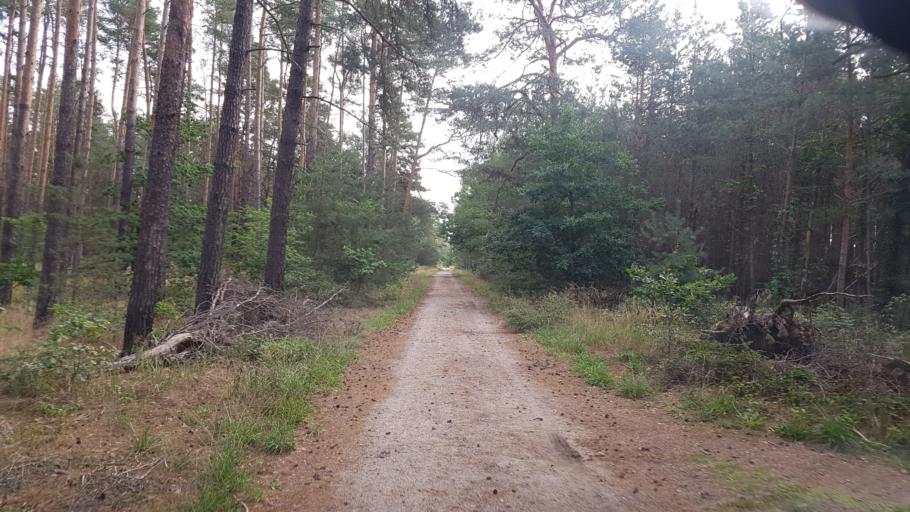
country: DE
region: Brandenburg
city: Ruckersdorf
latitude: 51.5769
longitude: 13.5803
